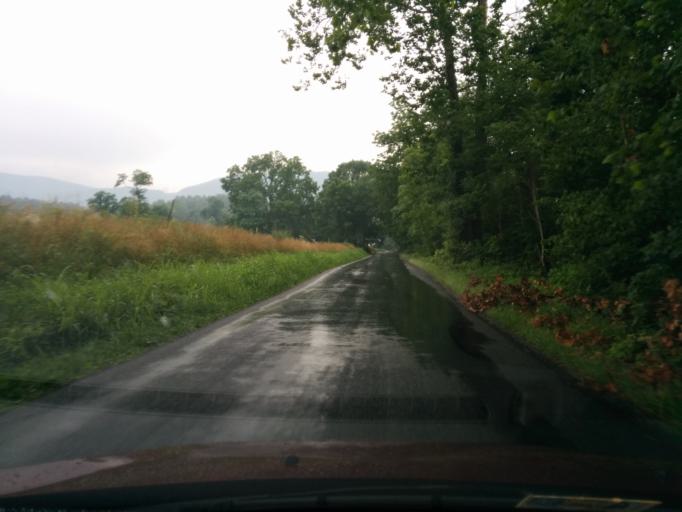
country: US
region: Virginia
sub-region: Rockbridge County
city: East Lexington
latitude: 37.9030
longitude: -79.4164
